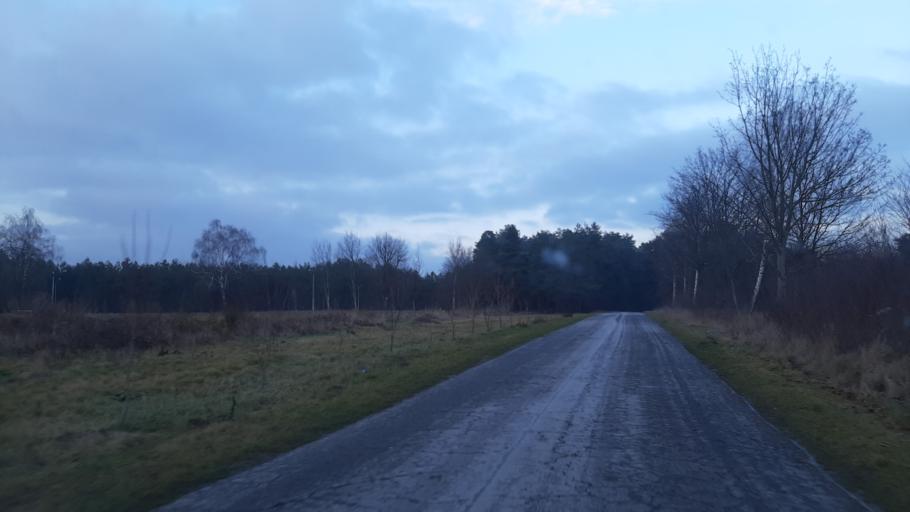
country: PL
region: Lublin Voivodeship
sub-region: Powiat lubartowski
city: Kamionka
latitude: 51.4780
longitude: 22.4689
